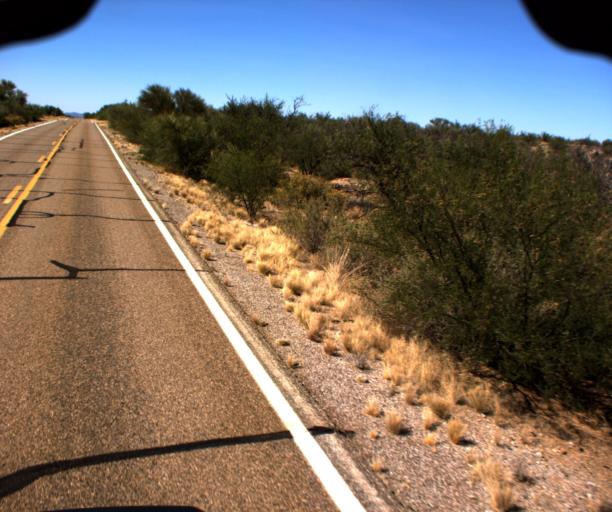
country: US
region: Arizona
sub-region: Pima County
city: Three Points
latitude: 31.9258
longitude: -111.3907
